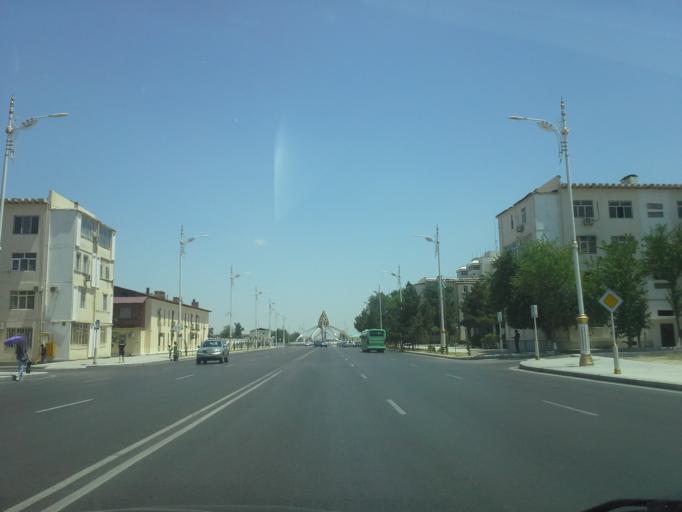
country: TM
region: Ahal
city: Ashgabat
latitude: 37.9231
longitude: 58.3851
